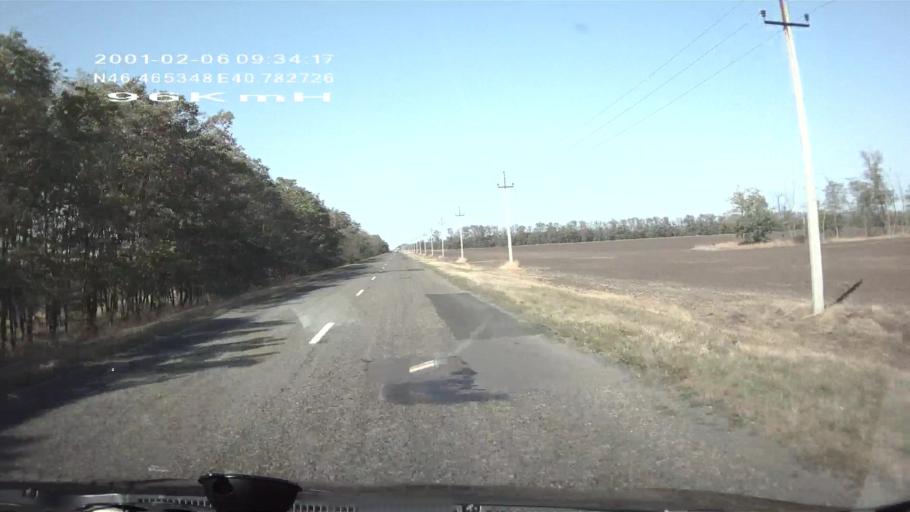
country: RU
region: Rostov
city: Yegorlykskaya
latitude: 46.4654
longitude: 40.7818
